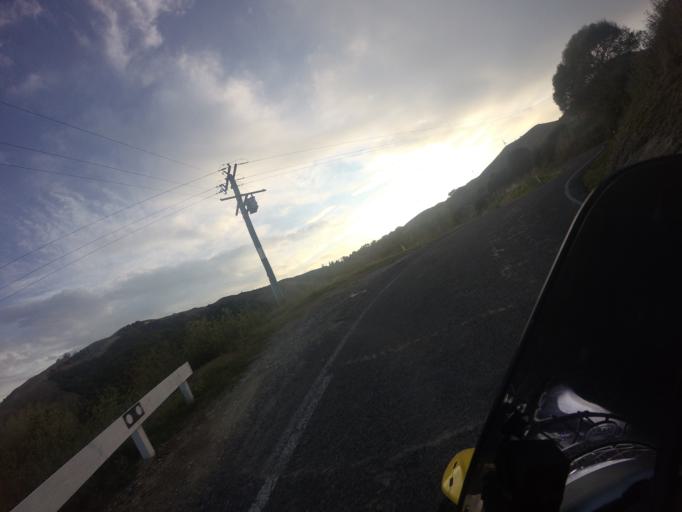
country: NZ
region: Gisborne
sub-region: Gisborne District
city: Gisborne
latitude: -38.6633
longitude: 178.0587
